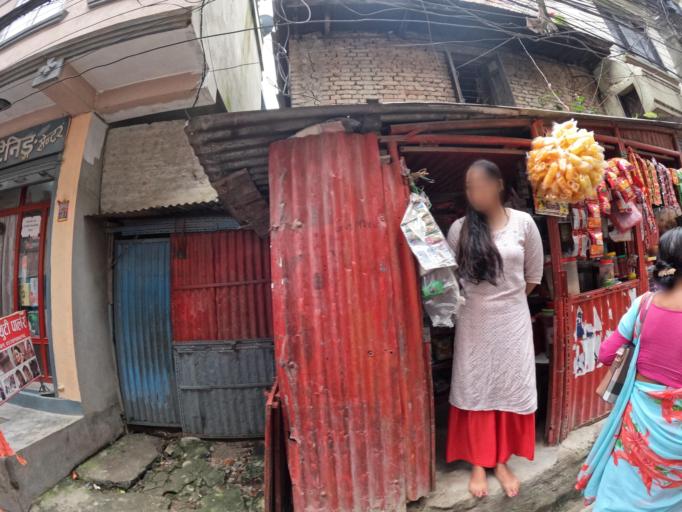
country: NP
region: Central Region
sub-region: Bagmati Zone
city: Kathmandu
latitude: 27.7363
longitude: 85.3114
